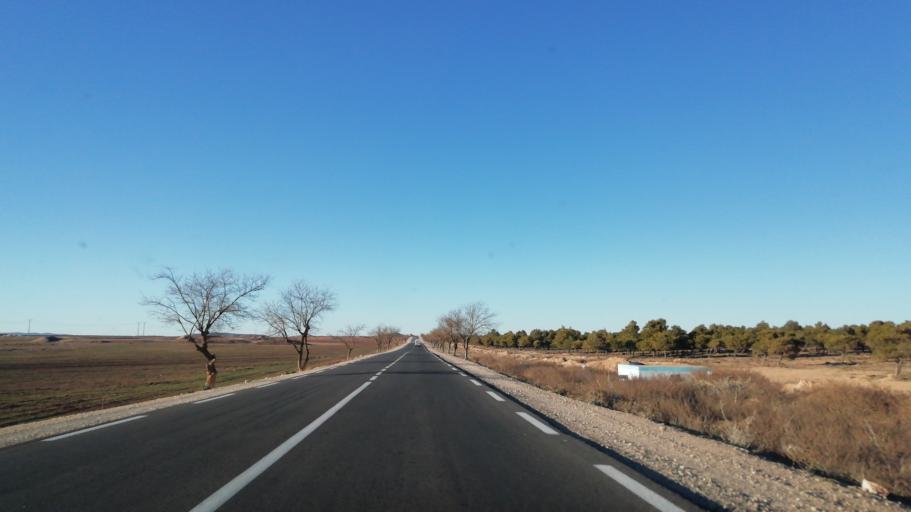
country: DZ
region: Tlemcen
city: Sebdou
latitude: 34.5318
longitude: -1.2958
